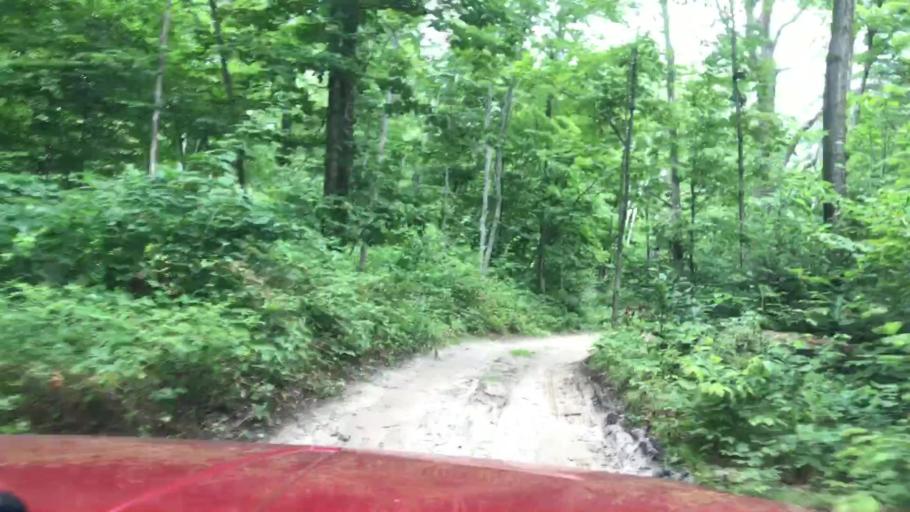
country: US
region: Michigan
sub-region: Charlevoix County
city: Charlevoix
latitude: 45.7248
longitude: -85.5644
